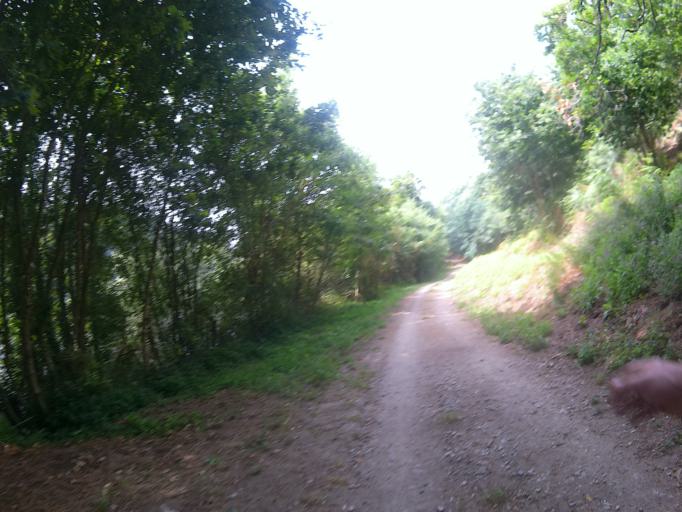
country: PT
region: Viana do Castelo
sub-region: Ponte de Lima
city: Ponte de Lima
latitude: 41.7797
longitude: -8.5525
